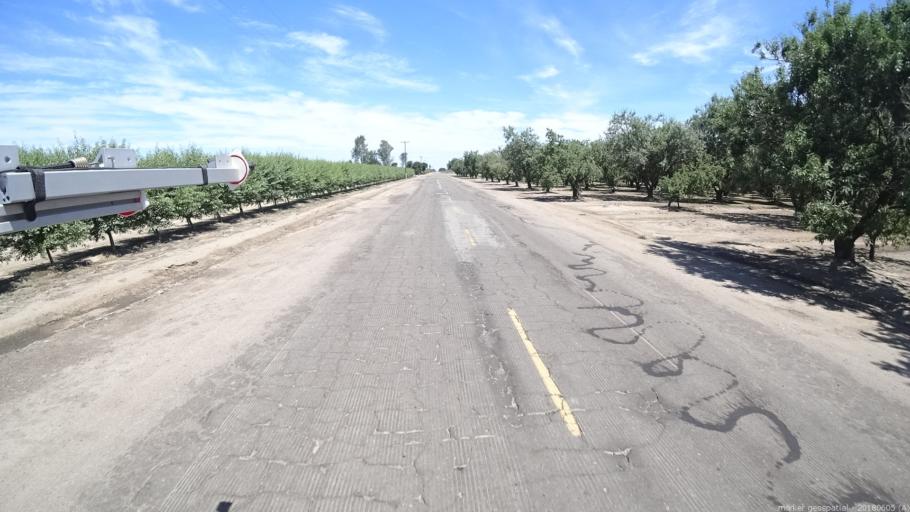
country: US
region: California
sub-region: Madera County
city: Chowchilla
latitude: 37.0672
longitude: -120.4372
